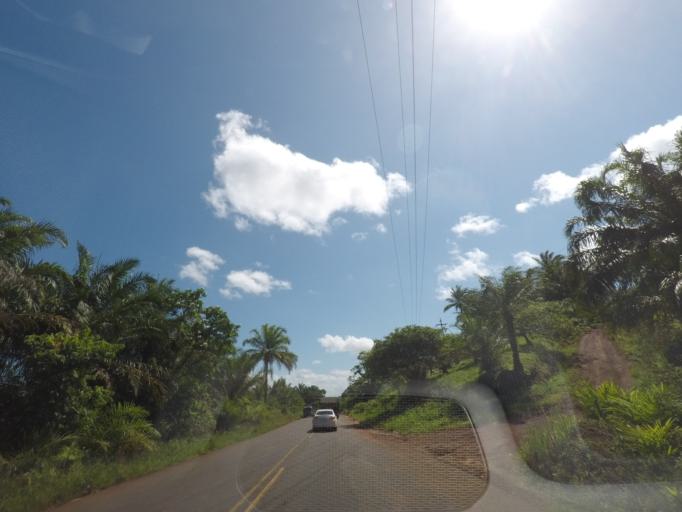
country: BR
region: Bahia
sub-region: Itubera
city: Itubera
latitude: -13.6693
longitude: -39.1215
